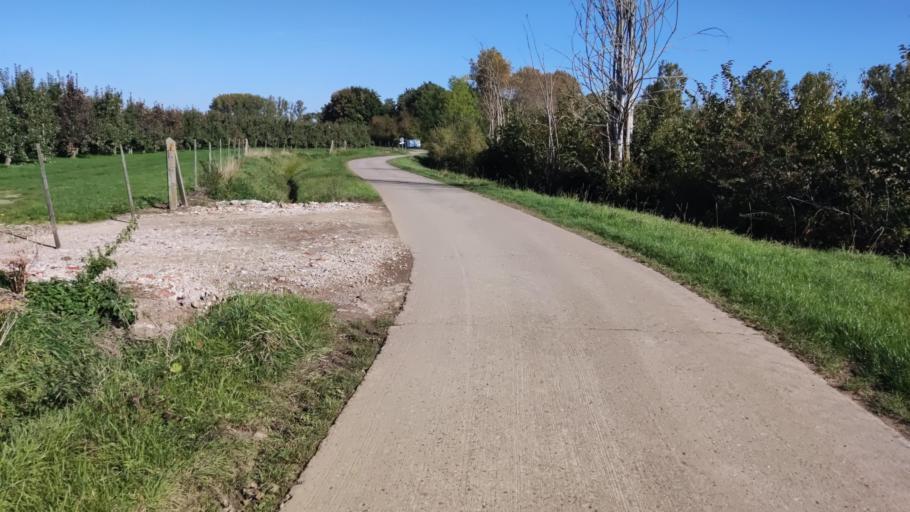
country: BE
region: Flanders
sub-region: Provincie Vlaams-Brabant
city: Zoutleeuw
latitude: 50.8278
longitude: 5.0824
